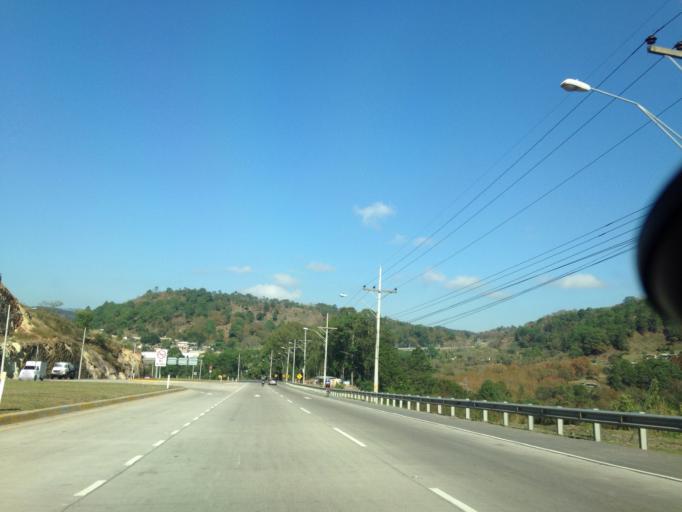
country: HN
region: Francisco Morazan
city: El Lolo
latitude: 14.1385
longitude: -87.2753
